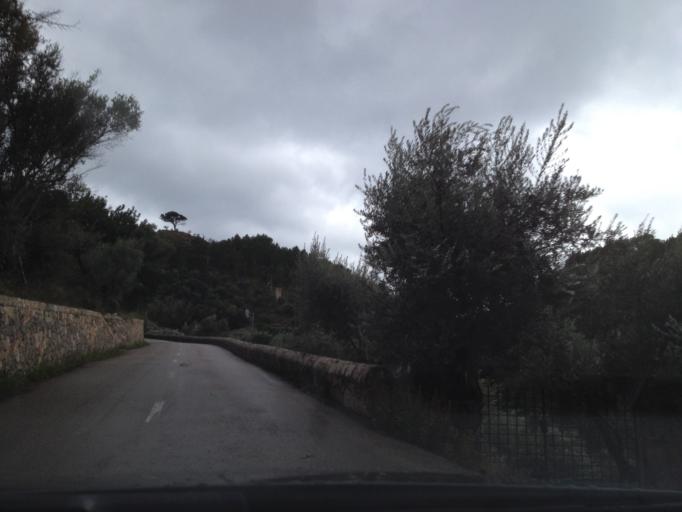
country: ES
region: Balearic Islands
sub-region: Illes Balears
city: Soller
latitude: 39.7728
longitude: 2.6798
